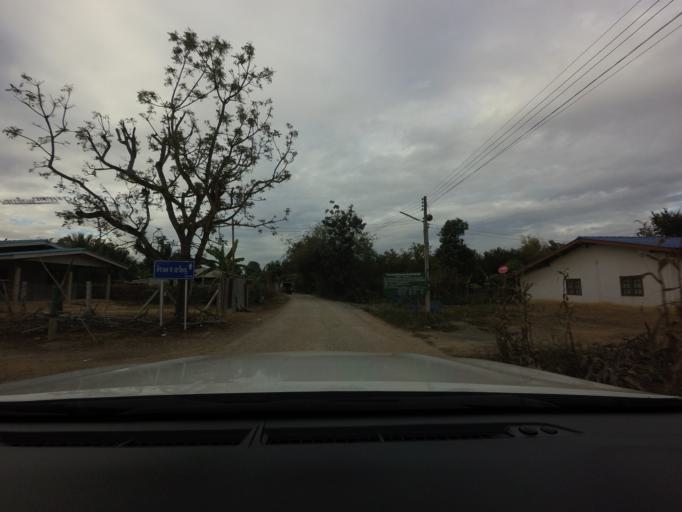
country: TH
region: Nakhon Ratchasima
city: Wang Nam Khiao
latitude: 14.4656
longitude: 101.6605
